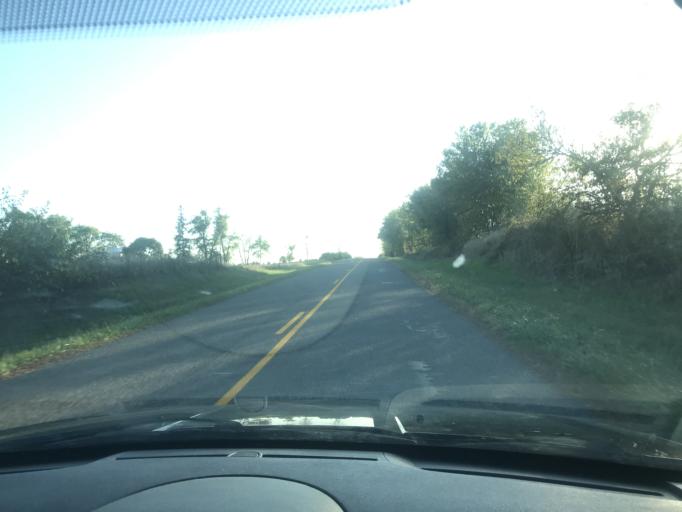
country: US
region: Ohio
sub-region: Logan County
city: De Graff
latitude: 40.2683
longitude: -83.8540
